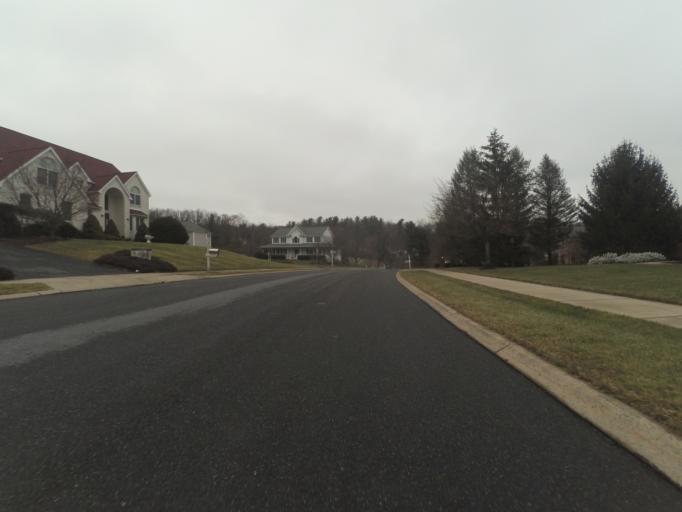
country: US
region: Pennsylvania
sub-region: Centre County
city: Park Forest Village
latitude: 40.7879
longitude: -77.9130
